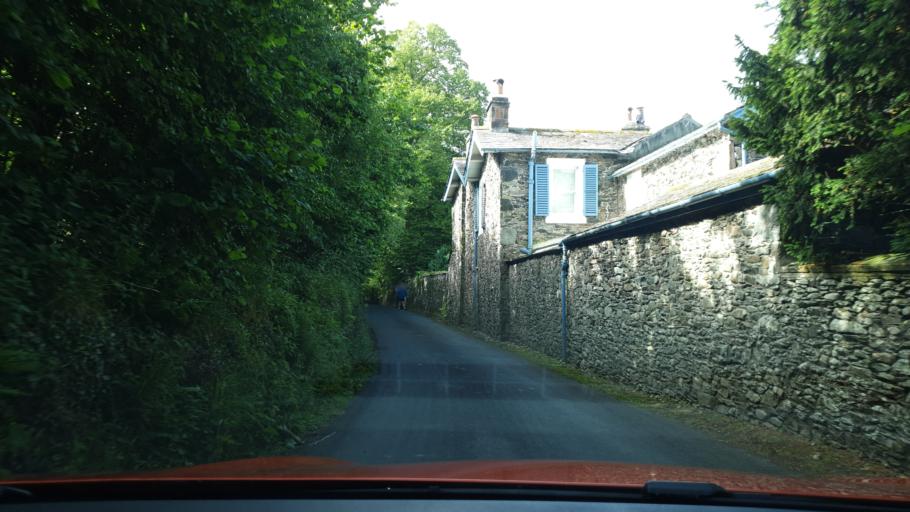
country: GB
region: England
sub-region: Cumbria
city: Penrith
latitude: 54.5772
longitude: -2.8564
